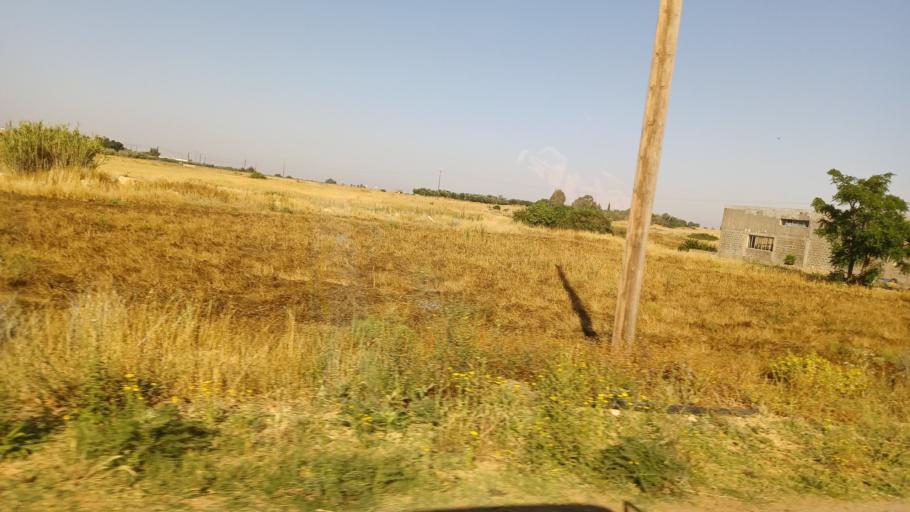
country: CY
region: Ammochostos
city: Frenaros
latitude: 35.0505
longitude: 33.9177
